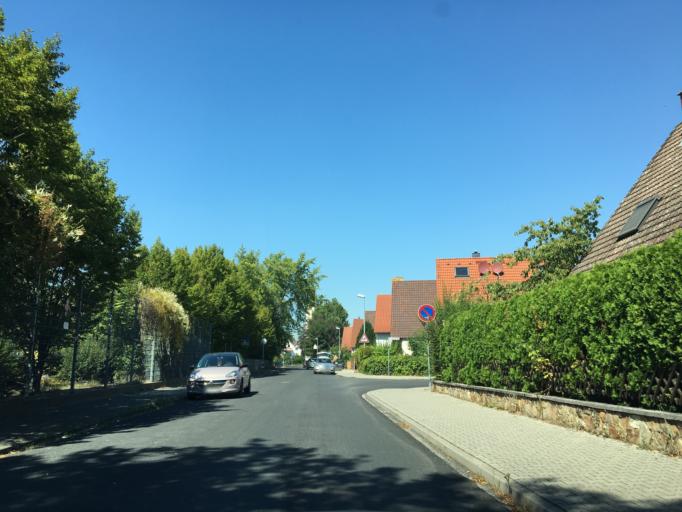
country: DE
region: Hesse
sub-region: Regierungsbezirk Darmstadt
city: Russelsheim
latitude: 49.9995
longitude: 8.4321
